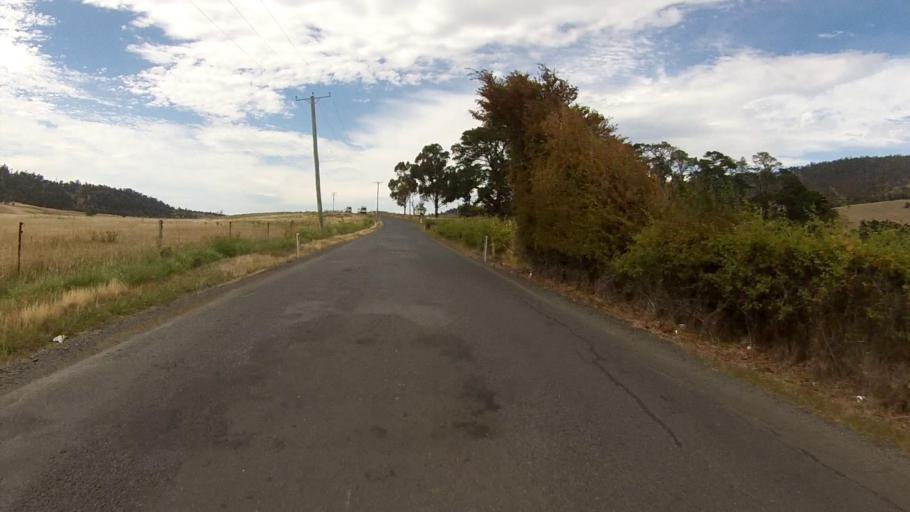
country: AU
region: Tasmania
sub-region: Brighton
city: Old Beach
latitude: -42.7264
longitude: 147.3436
